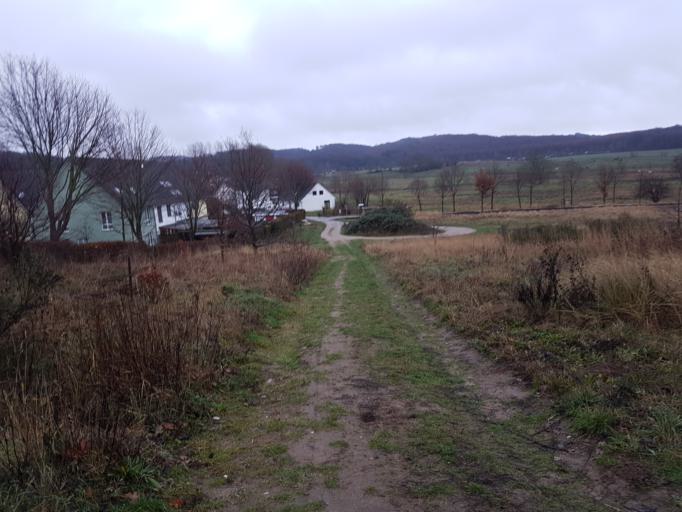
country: DE
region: Mecklenburg-Vorpommern
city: Ostseebad Binz
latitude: 54.3922
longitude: 13.6038
